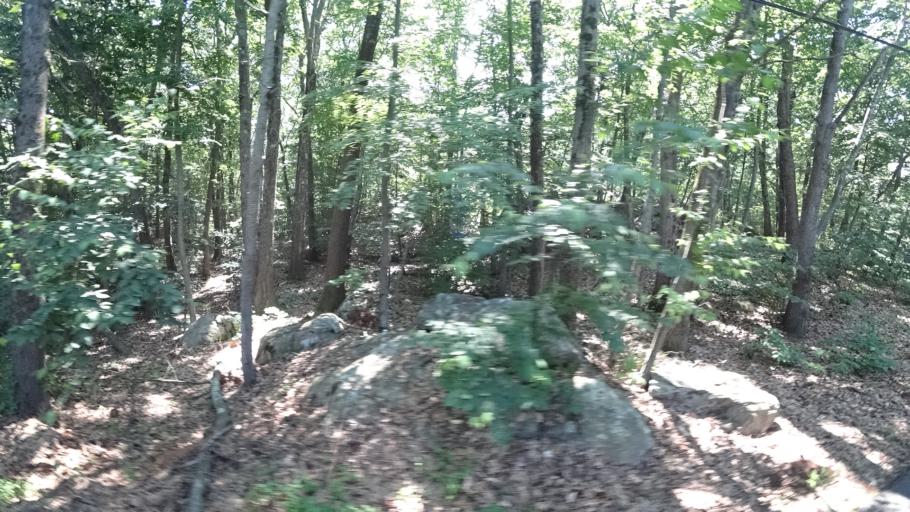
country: US
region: Massachusetts
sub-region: Norfolk County
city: Dedham
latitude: 42.2428
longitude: -71.1870
